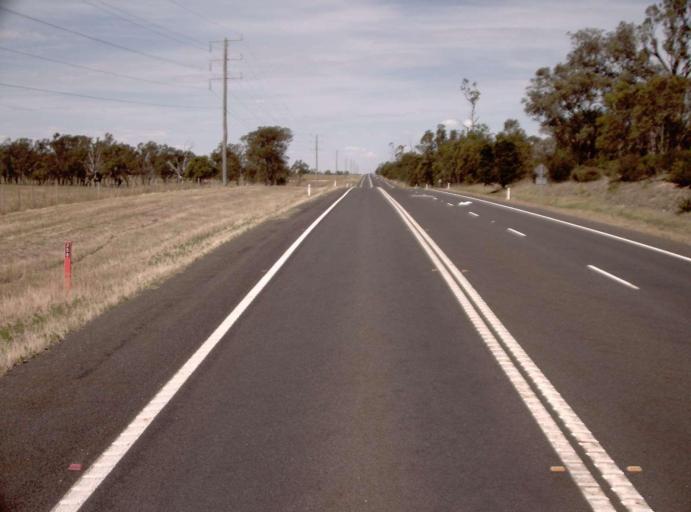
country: AU
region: Victoria
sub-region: East Gippsland
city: Bairnsdale
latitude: -37.8907
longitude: 147.3854
